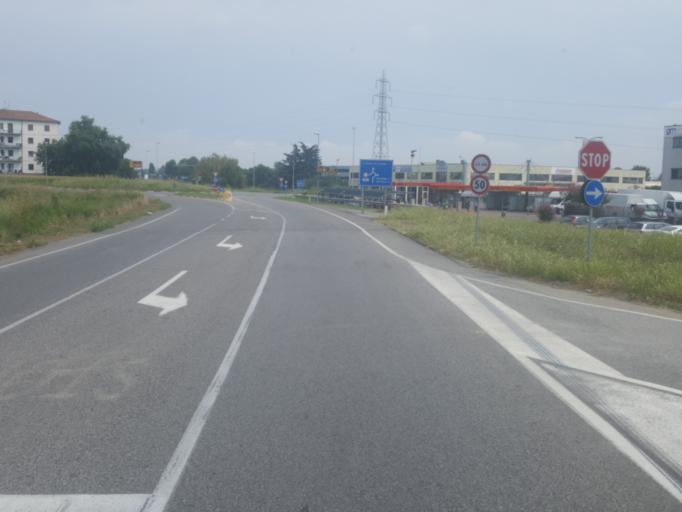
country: IT
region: Lombardy
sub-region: Citta metropolitana di Milano
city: Melzo
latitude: 45.4809
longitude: 9.4365
